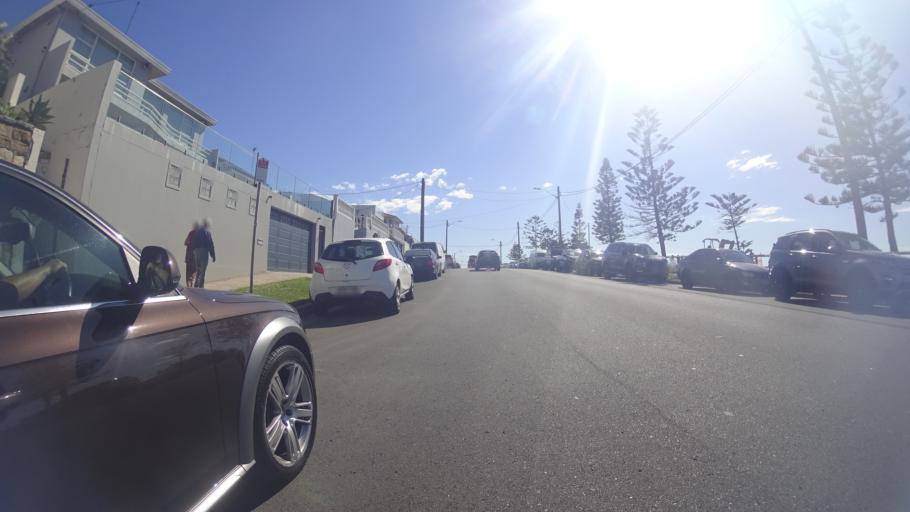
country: AU
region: New South Wales
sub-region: Randwick
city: South Coogee
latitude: -33.9447
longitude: 151.2608
